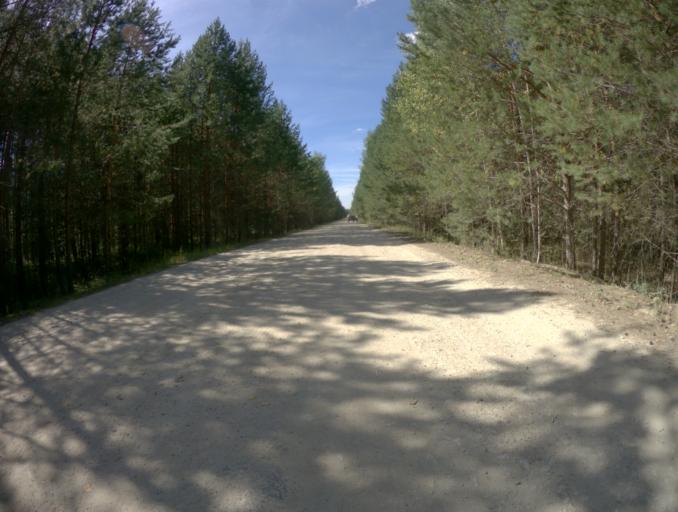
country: RU
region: Vladimir
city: Zolotkovo
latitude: 55.5969
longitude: 41.1819
